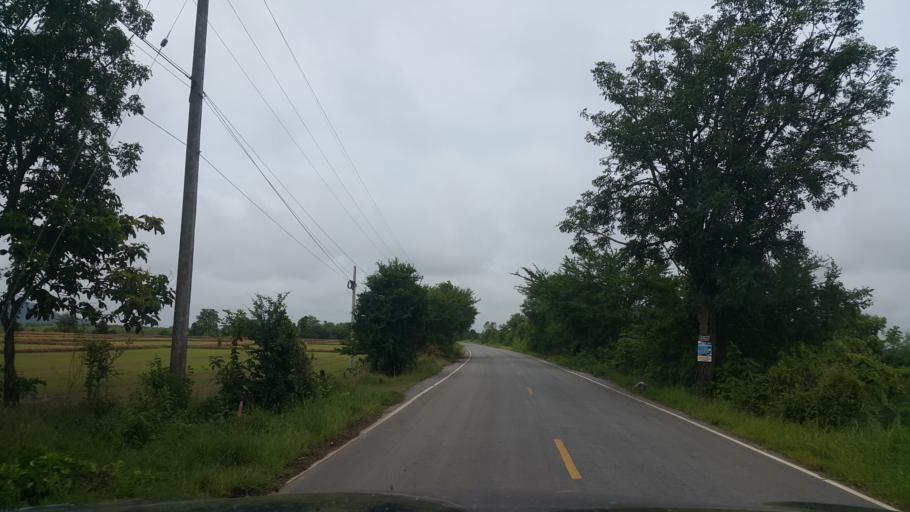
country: TH
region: Sukhothai
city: Sawankhalok
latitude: 17.3125
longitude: 99.6994
